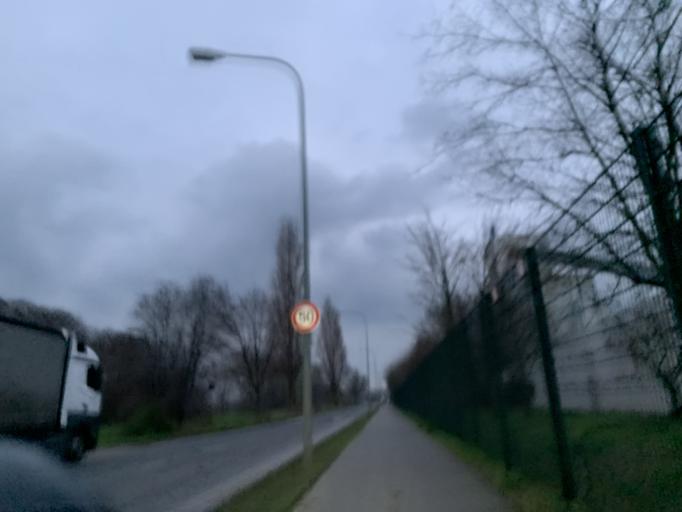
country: DE
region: North Rhine-Westphalia
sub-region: Regierungsbezirk Dusseldorf
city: Meerbusch
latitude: 51.3342
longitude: 6.6939
